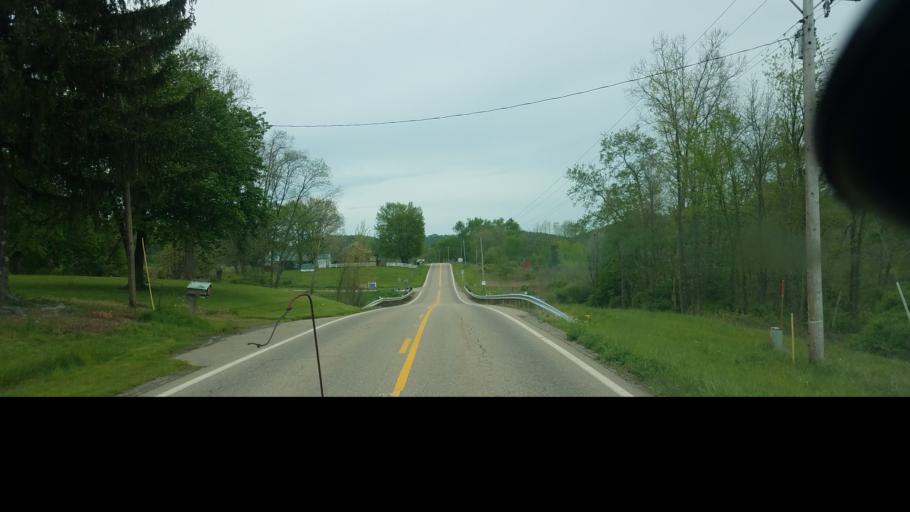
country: US
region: Ohio
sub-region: Tuscarawas County
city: Newcomerstown
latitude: 40.2574
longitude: -81.5122
